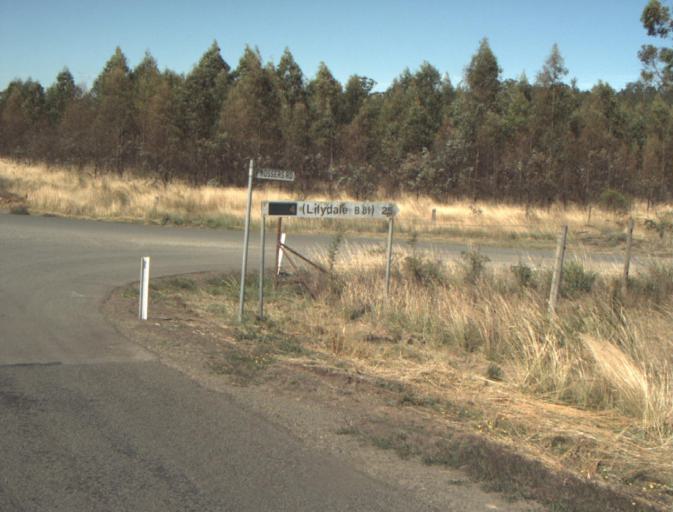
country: AU
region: Tasmania
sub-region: Launceston
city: Newstead
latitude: -41.3794
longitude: 147.2969
